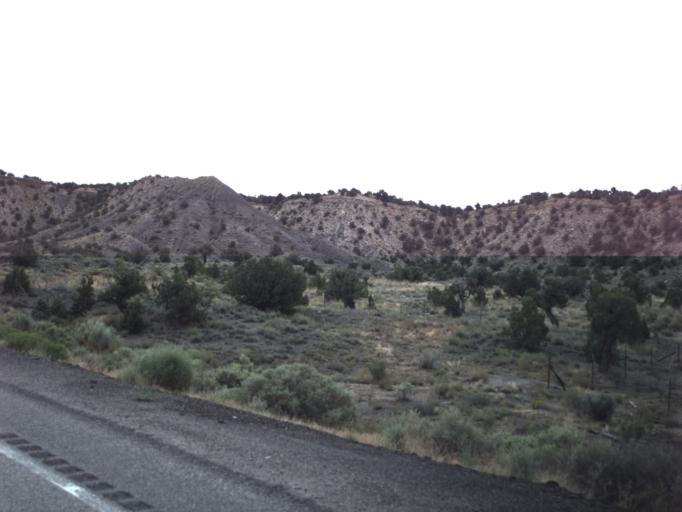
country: US
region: Utah
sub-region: Carbon County
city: Wellington
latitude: 39.5471
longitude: -110.6461
